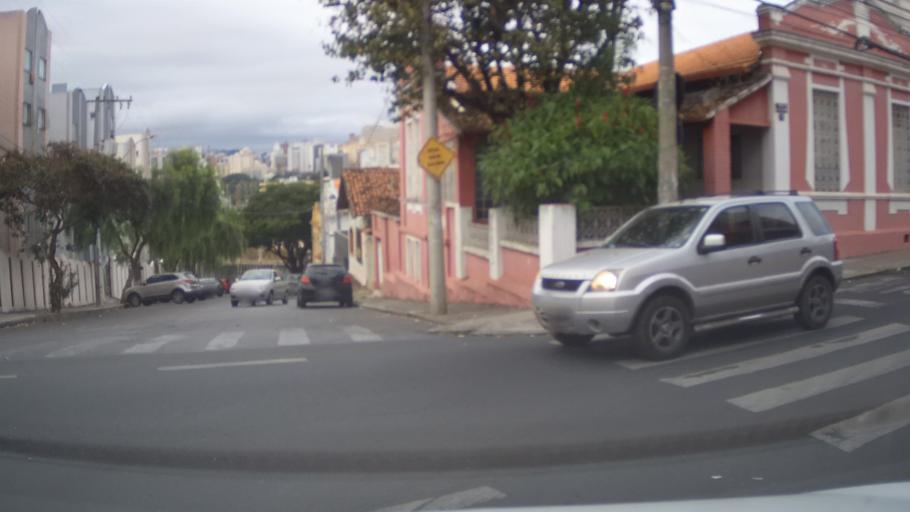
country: BR
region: Minas Gerais
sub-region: Belo Horizonte
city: Belo Horizonte
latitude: -19.9123
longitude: -43.9327
